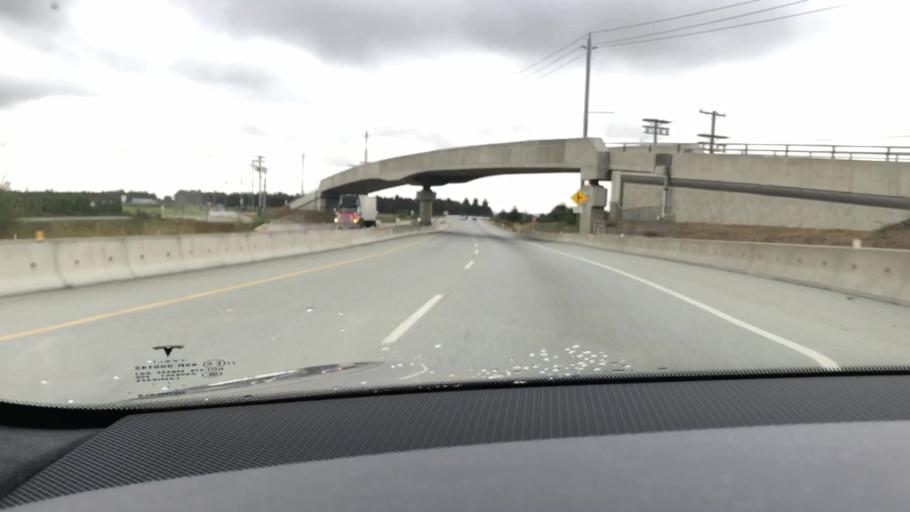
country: CA
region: British Columbia
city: Ladner
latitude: 49.1238
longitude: -123.0235
